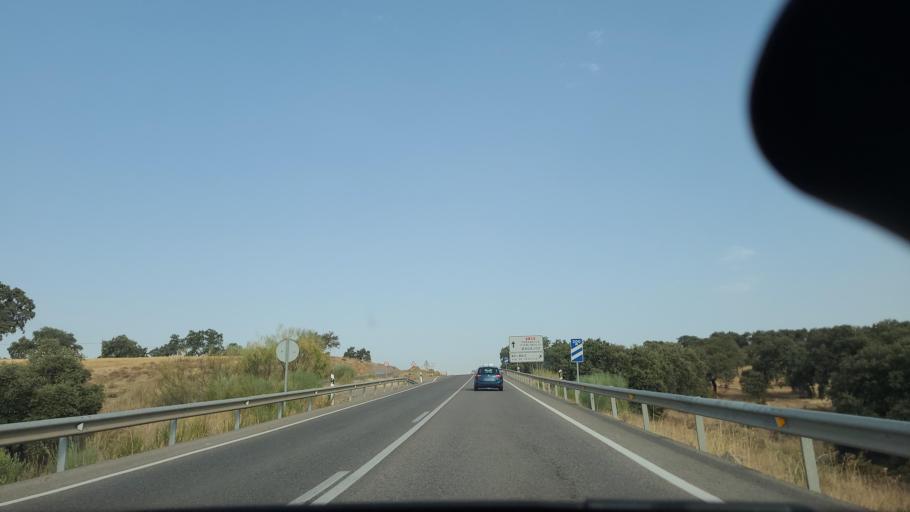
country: ES
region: Andalusia
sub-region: Province of Cordoba
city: Belmez
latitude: 38.2857
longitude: -5.2171
